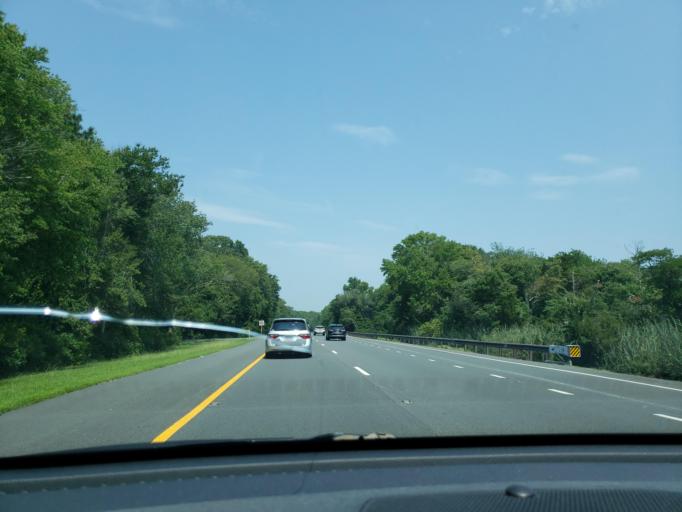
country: US
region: New Jersey
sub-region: Cape May County
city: Avalon
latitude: 39.1293
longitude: -74.7695
